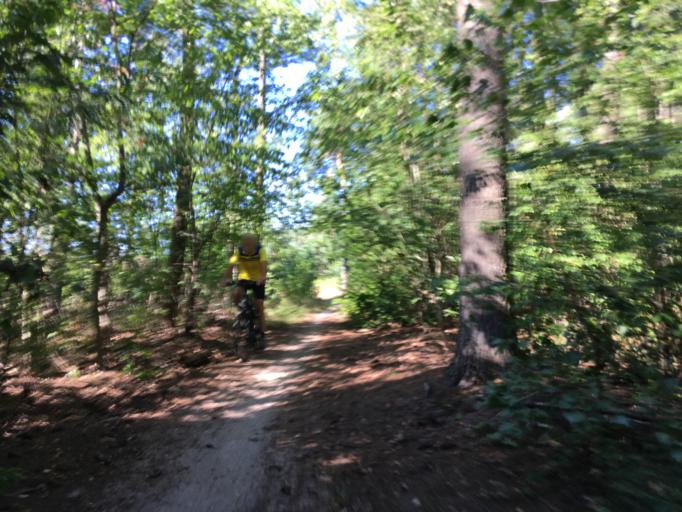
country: DE
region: Brandenburg
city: Schulzendorf
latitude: 52.3773
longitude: 13.5925
